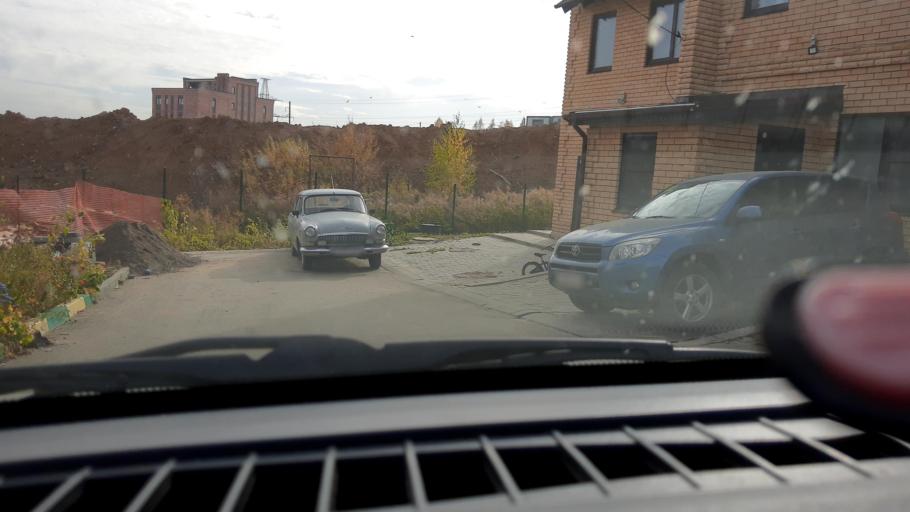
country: RU
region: Nizjnij Novgorod
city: Afonino
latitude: 56.2447
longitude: 44.0790
